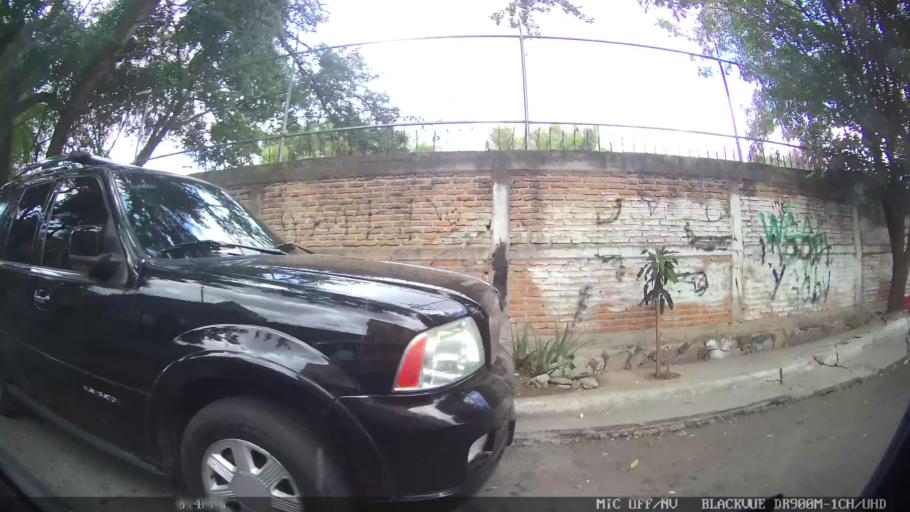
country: MX
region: Jalisco
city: Tlaquepaque
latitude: 20.6596
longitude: -103.2808
